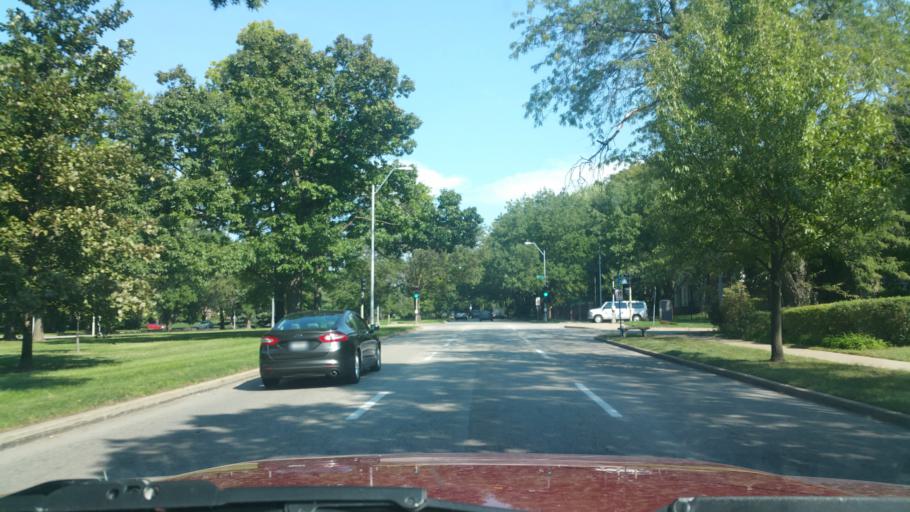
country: US
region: Kansas
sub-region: Johnson County
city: Mission Hills
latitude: 39.0202
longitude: -94.6016
